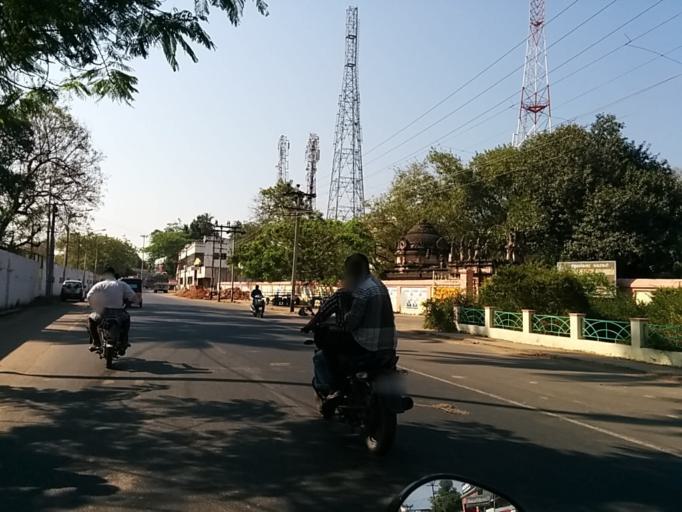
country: IN
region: Pondicherry
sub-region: Puducherry
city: Puducherry
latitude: 11.9546
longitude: 79.8281
